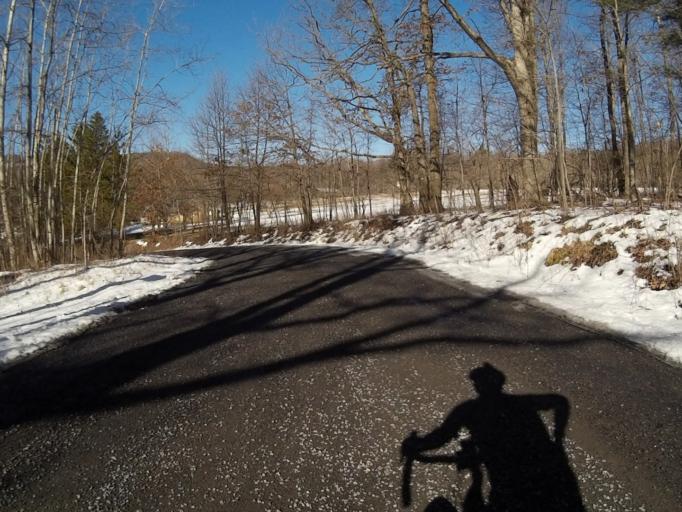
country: US
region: Pennsylvania
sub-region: Centre County
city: Stormstown
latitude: 40.8515
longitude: -78.0451
